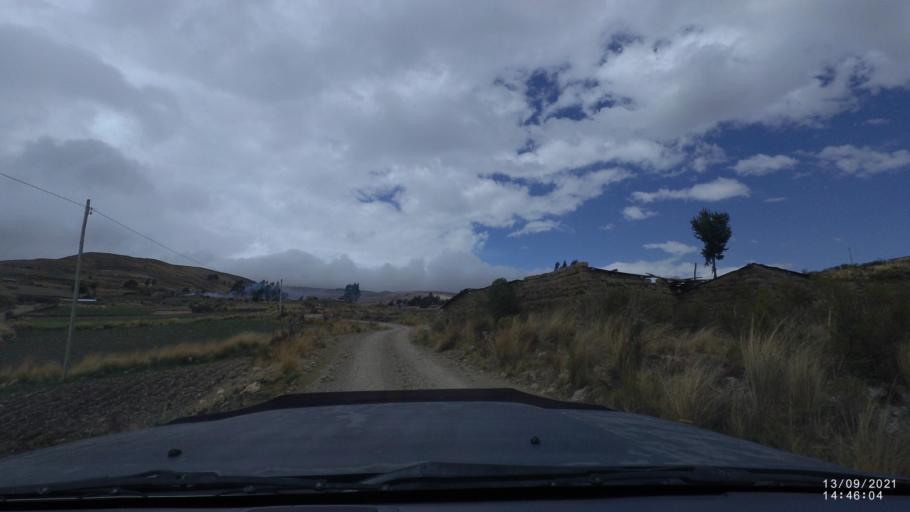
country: BO
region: Cochabamba
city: Colomi
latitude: -17.3513
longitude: -65.8058
